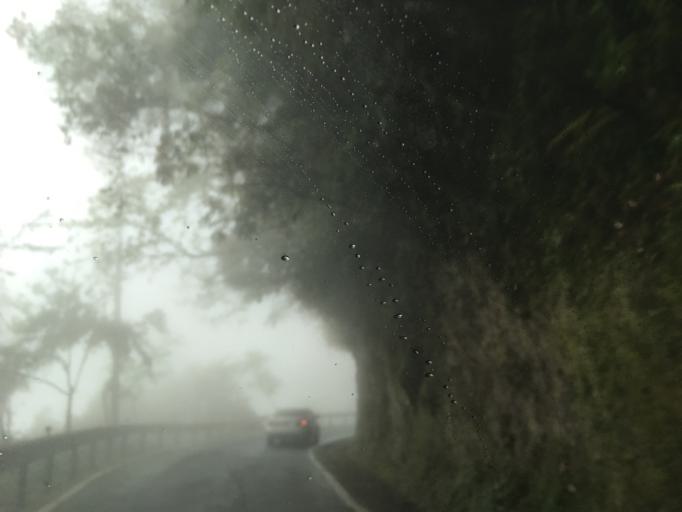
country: TW
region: Taiwan
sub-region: Hualien
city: Hualian
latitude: 24.1876
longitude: 121.4215
